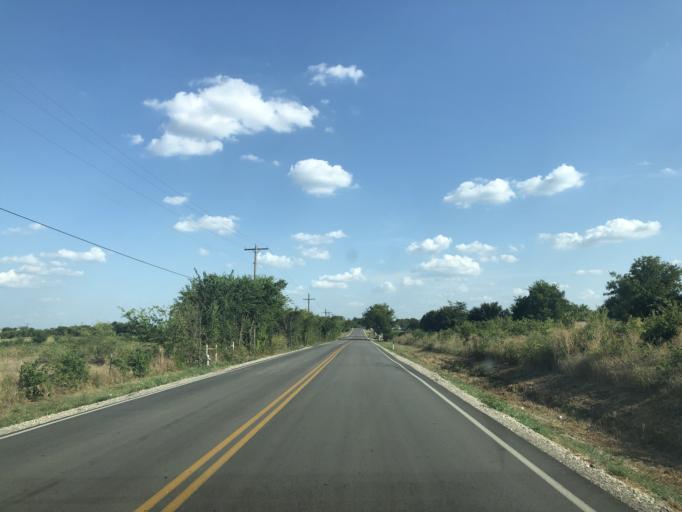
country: US
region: Texas
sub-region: Tarrant County
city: Eagle Mountain
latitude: 32.8973
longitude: -97.3981
